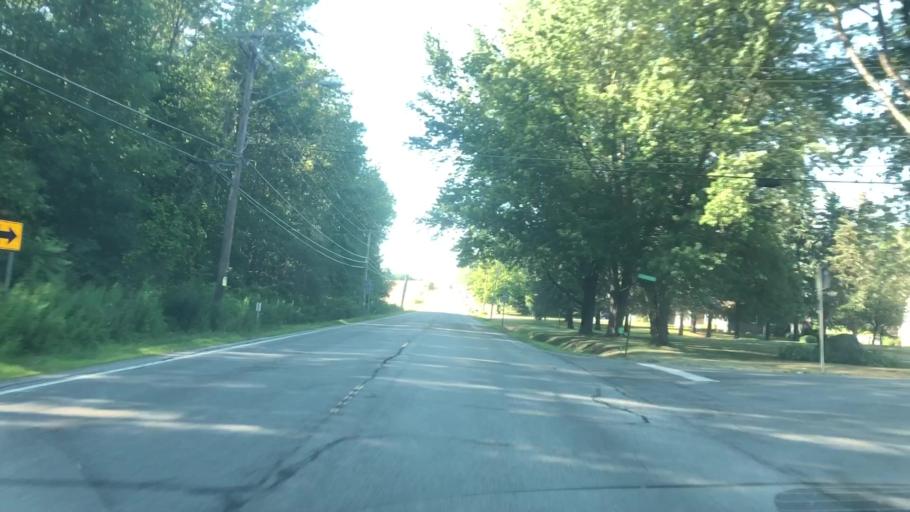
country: US
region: New York
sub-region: Wayne County
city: Macedon
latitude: 43.1312
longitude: -77.2926
